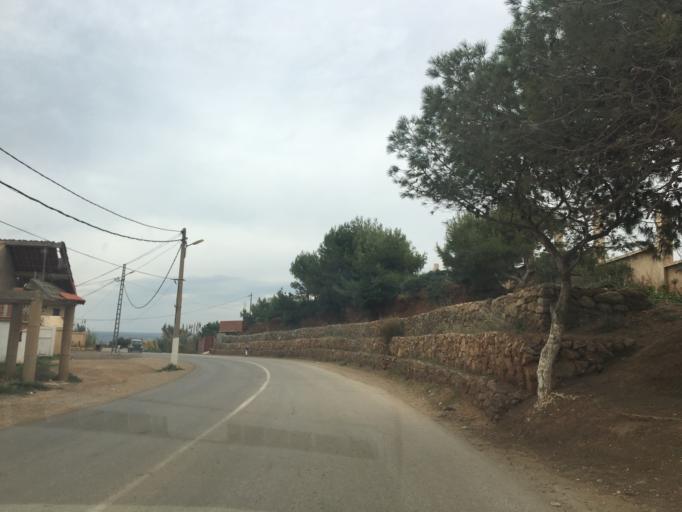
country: DZ
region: Tipaza
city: Tipasa
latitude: 36.6401
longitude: 2.3695
